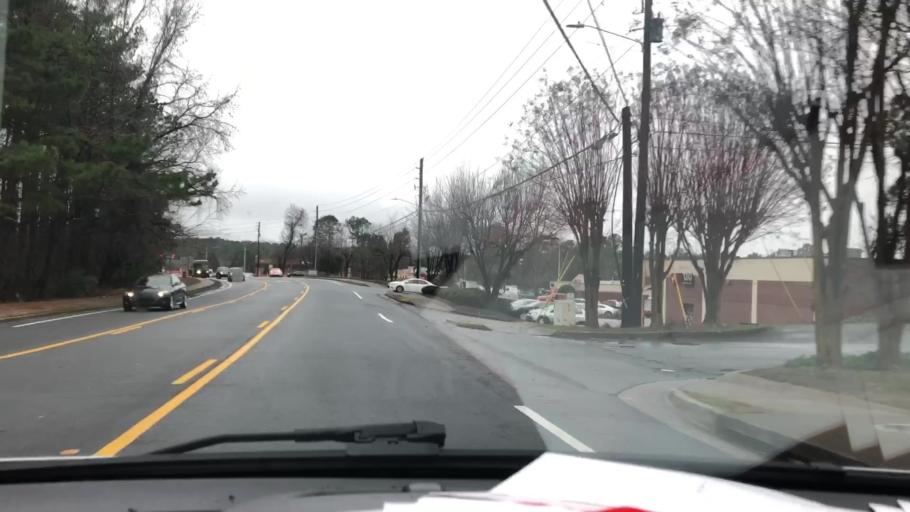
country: US
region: Georgia
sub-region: Gwinnett County
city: Norcross
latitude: 33.9692
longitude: -84.2186
